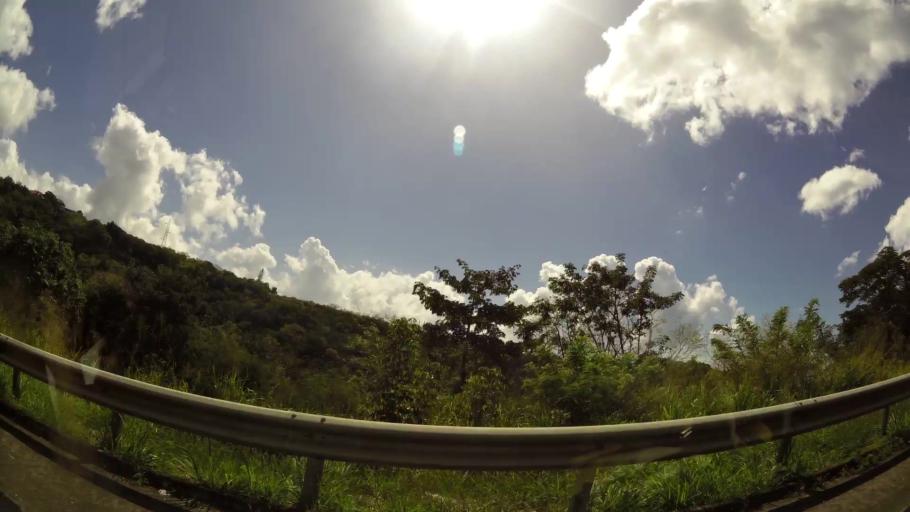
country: MQ
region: Martinique
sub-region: Martinique
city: Saint-Pierre
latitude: 14.6936
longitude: -61.1649
